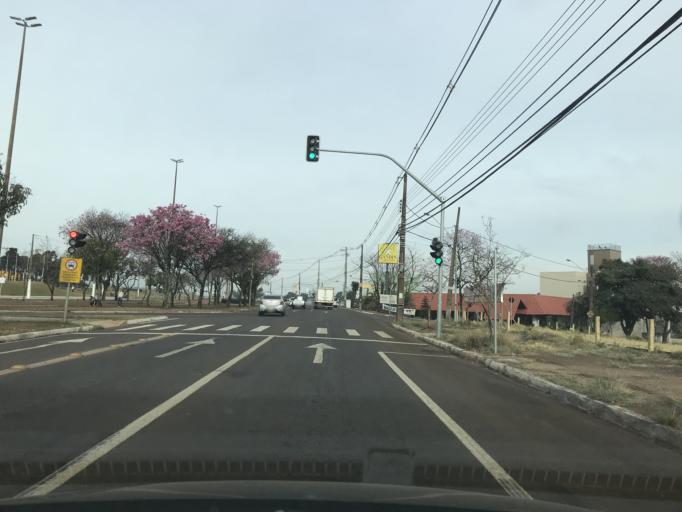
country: BR
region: Parana
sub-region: Cascavel
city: Cascavel
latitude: -24.9767
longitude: -53.4971
